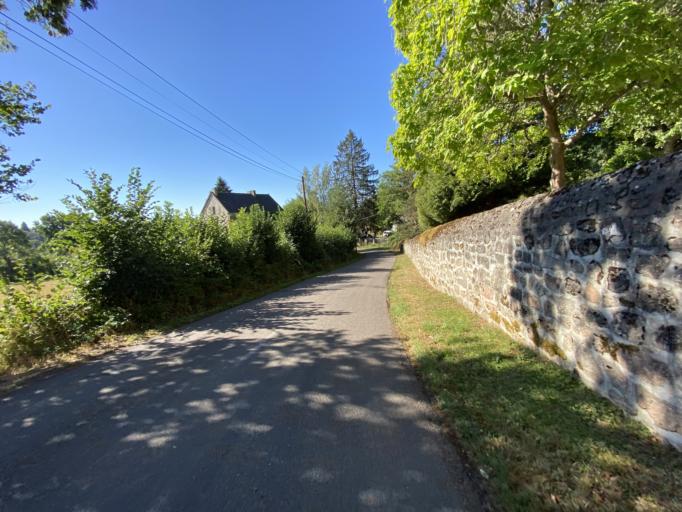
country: FR
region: Bourgogne
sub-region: Departement de la Cote-d'Or
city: Saulieu
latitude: 47.2637
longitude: 4.1759
